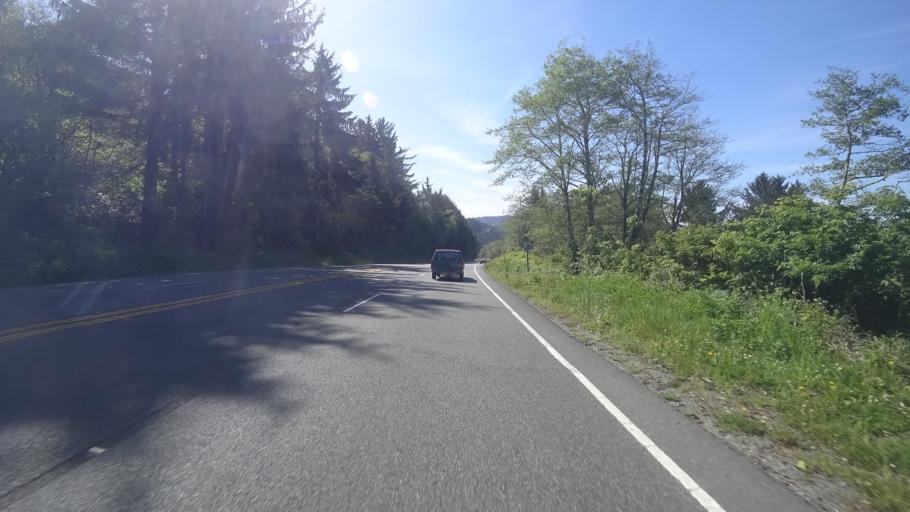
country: US
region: California
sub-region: Del Norte County
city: Bertsch-Oceanview
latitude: 41.6088
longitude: -124.1039
